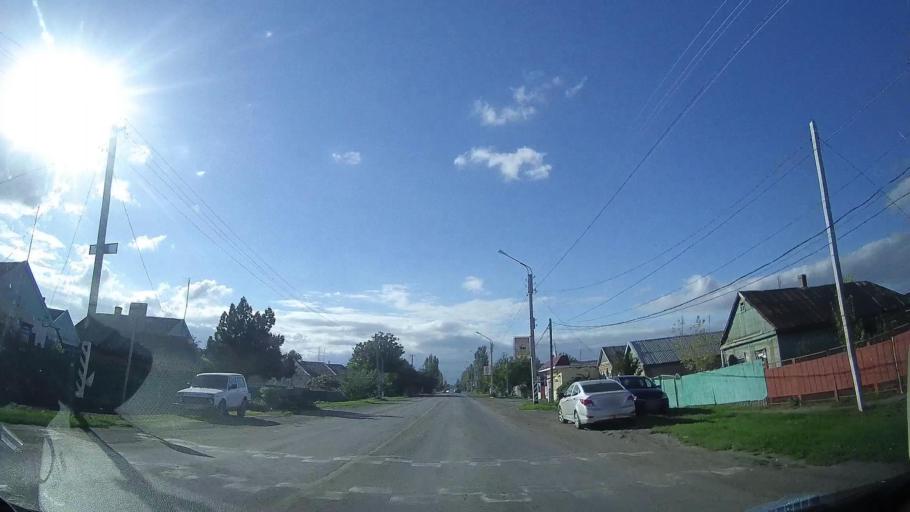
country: RU
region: Rostov
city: Tselina
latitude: 46.5310
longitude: 41.0184
